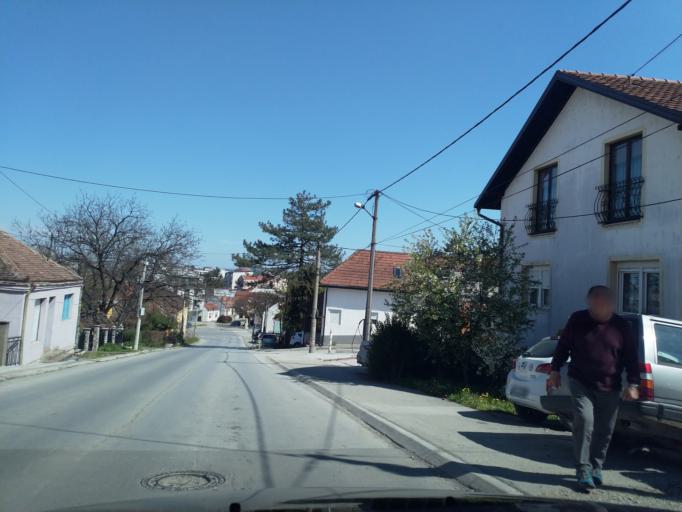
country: RS
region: Central Serbia
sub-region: Kolubarski Okrug
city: Valjevo
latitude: 44.2717
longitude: 19.8762
